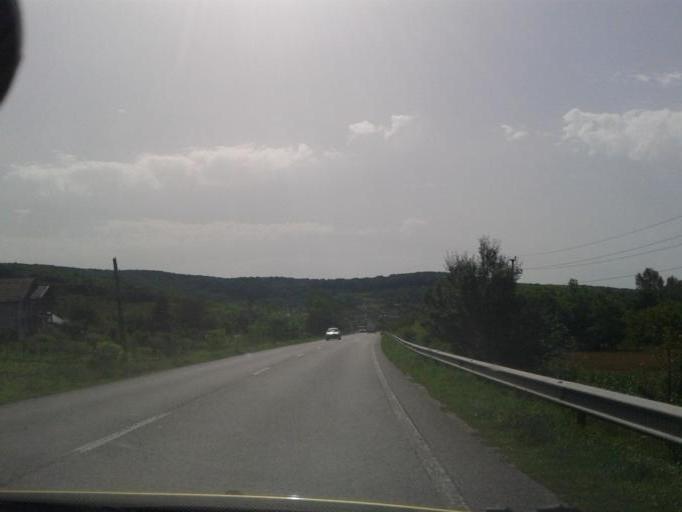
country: RO
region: Valcea
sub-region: Comuna Mihaesti
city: Mihaesti
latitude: 45.0628
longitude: 24.2405
